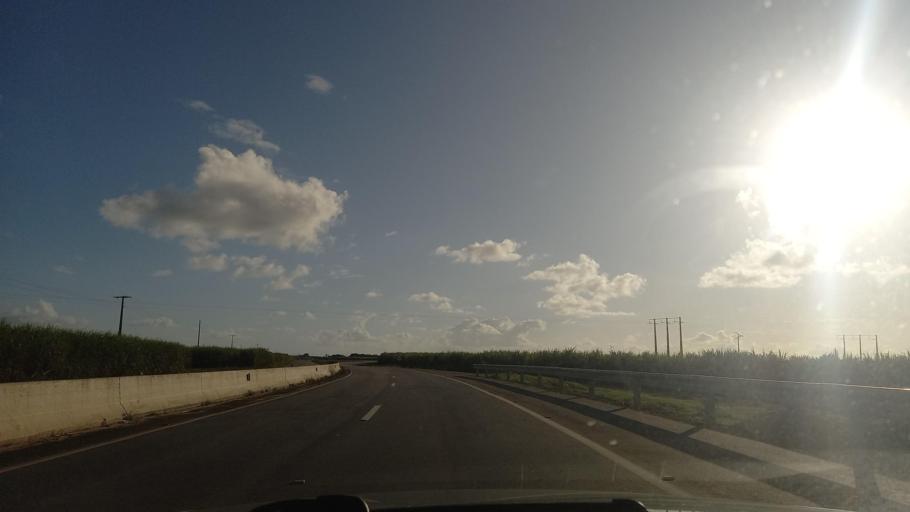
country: BR
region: Alagoas
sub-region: Sao Miguel Dos Campos
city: Sao Miguel dos Campos
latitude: -9.8009
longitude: -36.1924
